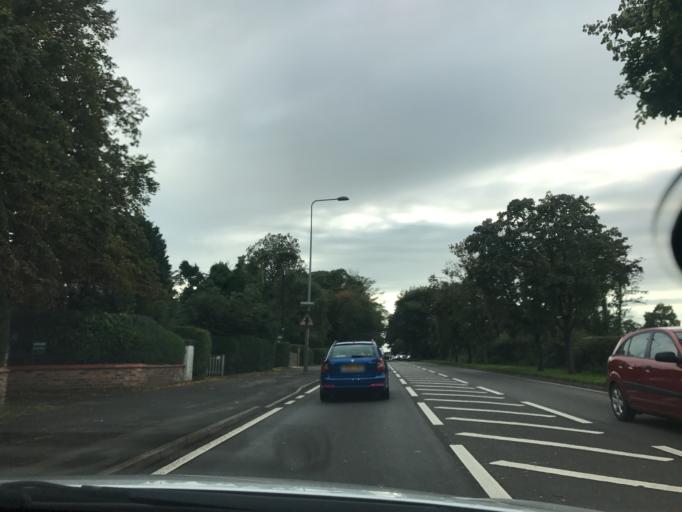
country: GB
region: England
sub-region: Cheshire West and Chester
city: Guilden Sutton
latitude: 53.1959
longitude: -2.8358
